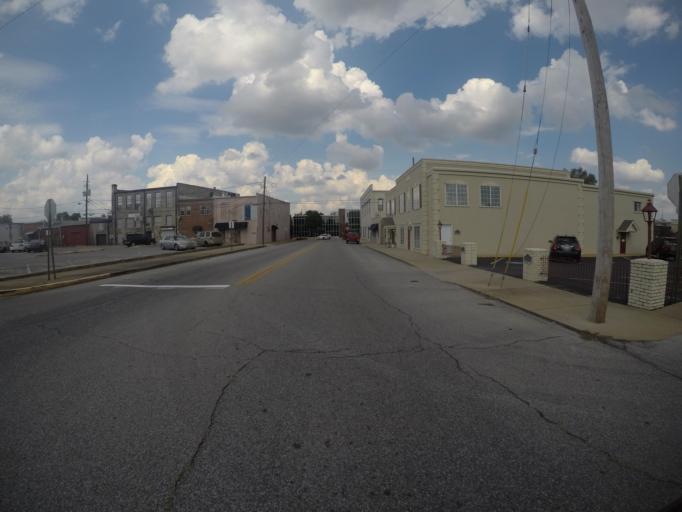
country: US
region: Arkansas
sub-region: Washington County
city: Springdale
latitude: 36.1843
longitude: -94.1313
